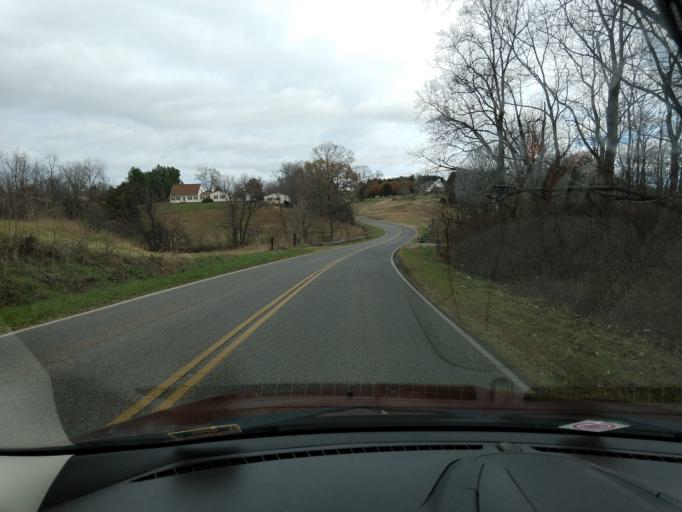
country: US
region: Virginia
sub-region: Franklin County
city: North Shore
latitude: 37.2331
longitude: -79.6711
